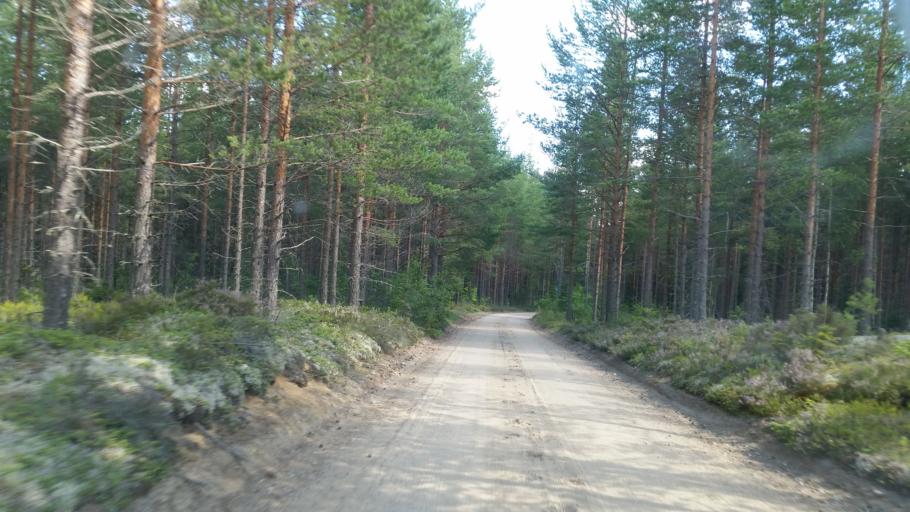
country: SE
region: Gaevleborg
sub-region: Ljusdals Kommun
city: Ljusdal
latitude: 61.9680
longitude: 16.2508
